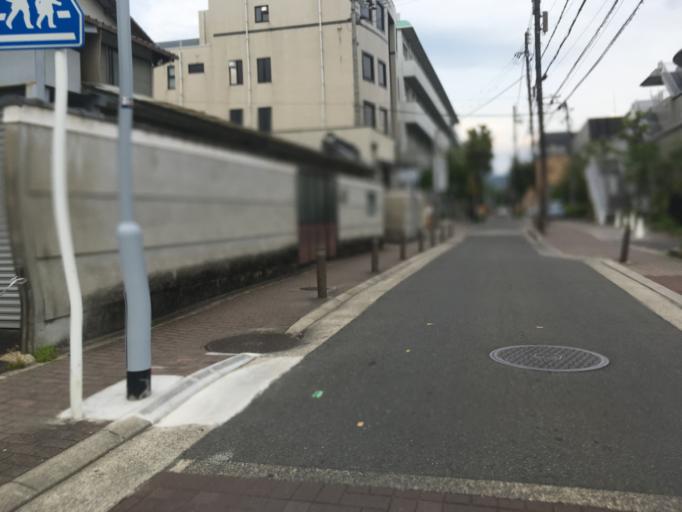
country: JP
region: Kyoto
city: Kyoto
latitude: 35.0250
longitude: 135.7551
